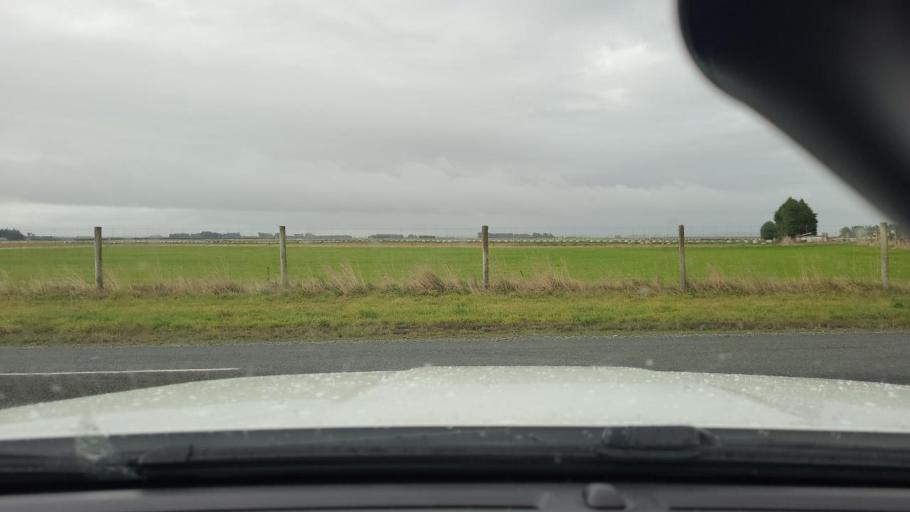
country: NZ
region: Southland
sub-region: Invercargill City
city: Invercargill
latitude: -46.3275
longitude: 168.2463
